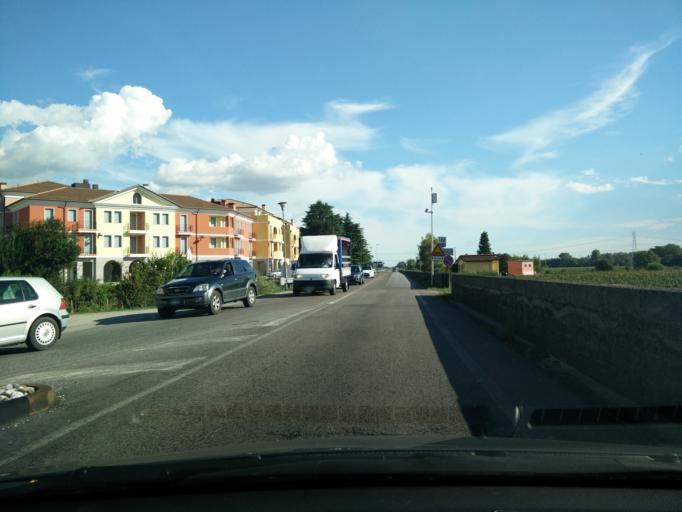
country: IT
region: Veneto
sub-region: Provincia di Treviso
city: Ponte di Piave
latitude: 45.7148
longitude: 12.4613
